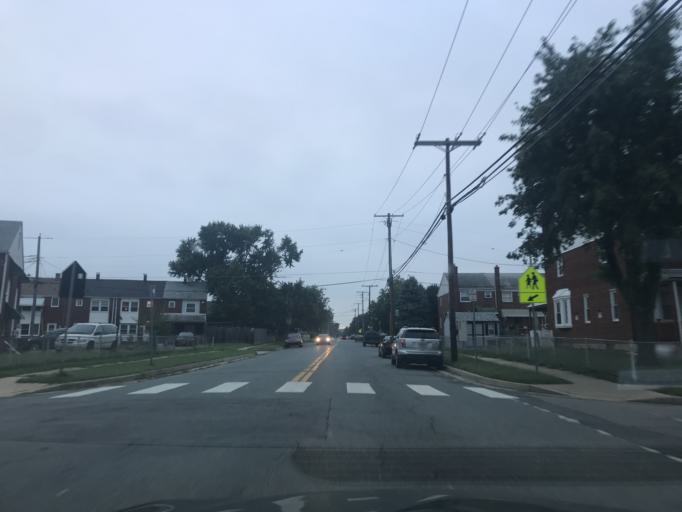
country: US
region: Maryland
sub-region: Baltimore County
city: Dundalk
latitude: 39.2578
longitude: -76.4874
